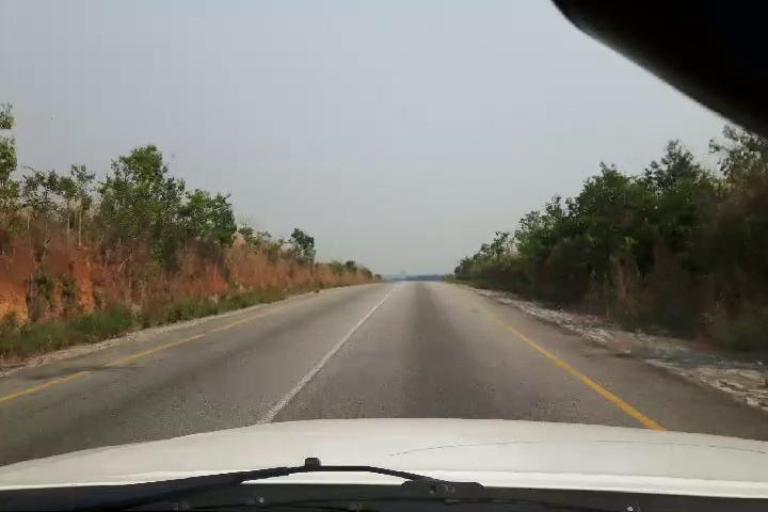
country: SL
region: Southern Province
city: Largo
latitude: 8.2280
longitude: -12.0778
